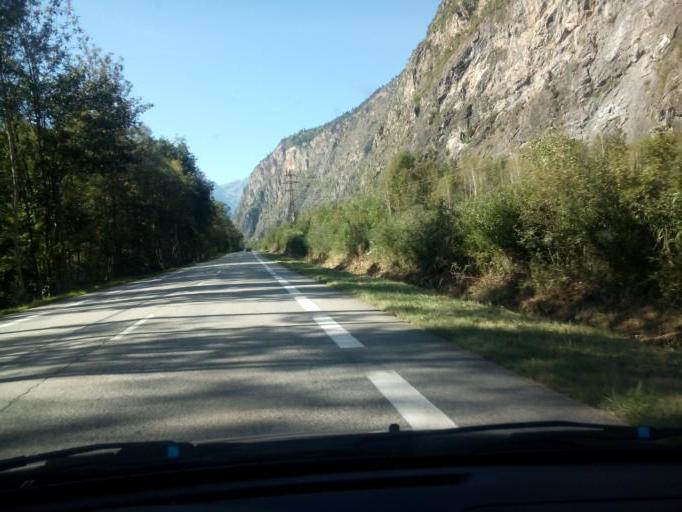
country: FR
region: Rhone-Alpes
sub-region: Departement de l'Isere
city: Huez
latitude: 45.0380
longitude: 6.0632
